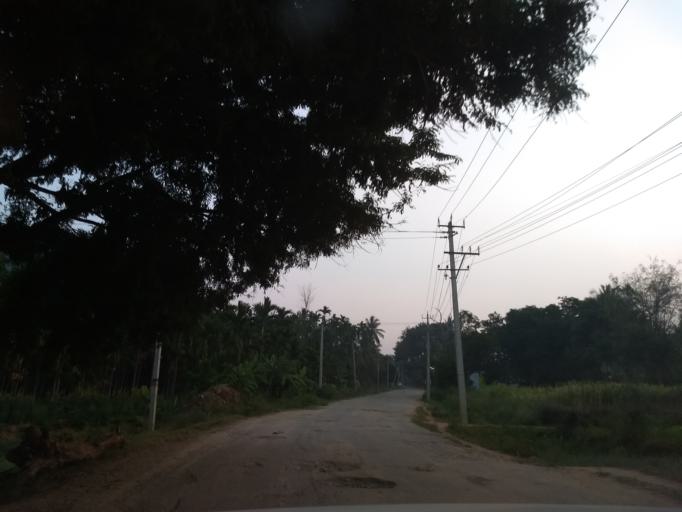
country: IN
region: Karnataka
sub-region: Tumkur
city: Tumkur
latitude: 13.3865
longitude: 77.2031
